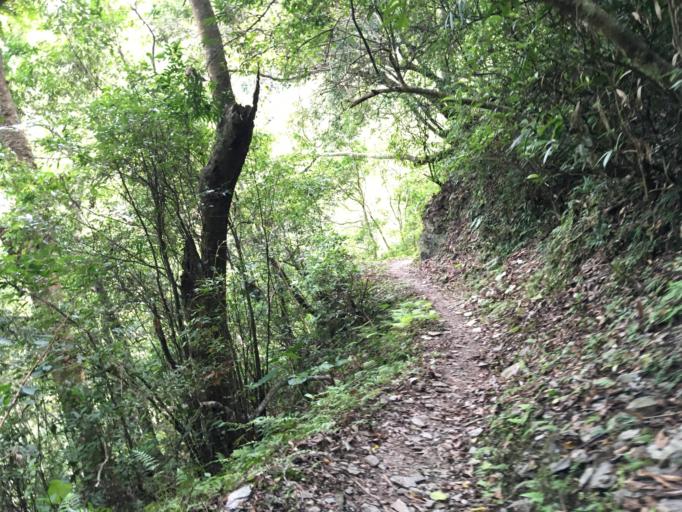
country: TW
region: Taiwan
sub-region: Yilan
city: Yilan
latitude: 24.4256
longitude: 121.7020
